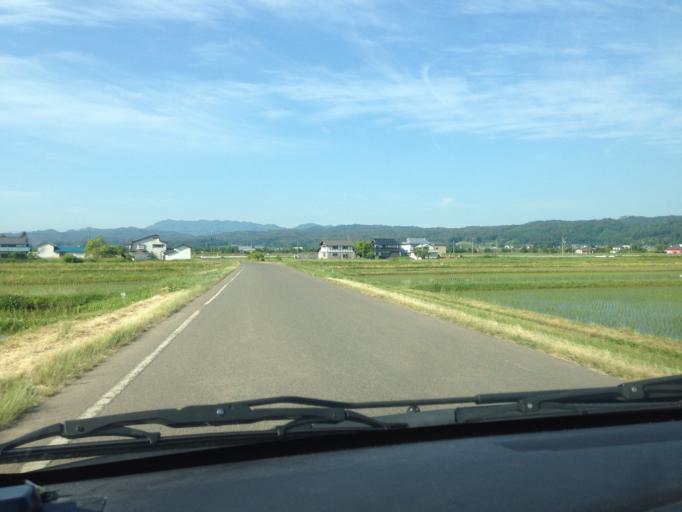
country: JP
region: Fukushima
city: Kitakata
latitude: 37.5452
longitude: 139.8150
